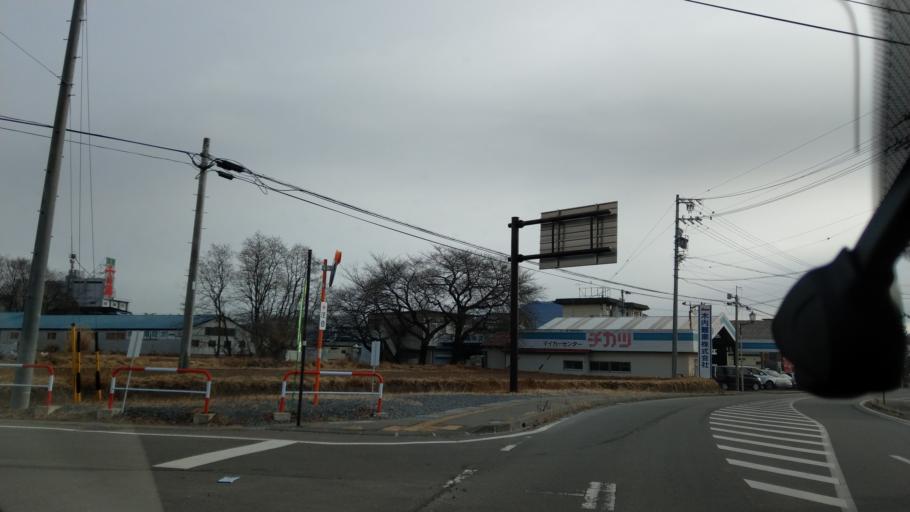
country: JP
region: Nagano
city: Komoro
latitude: 36.2858
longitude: 138.4618
